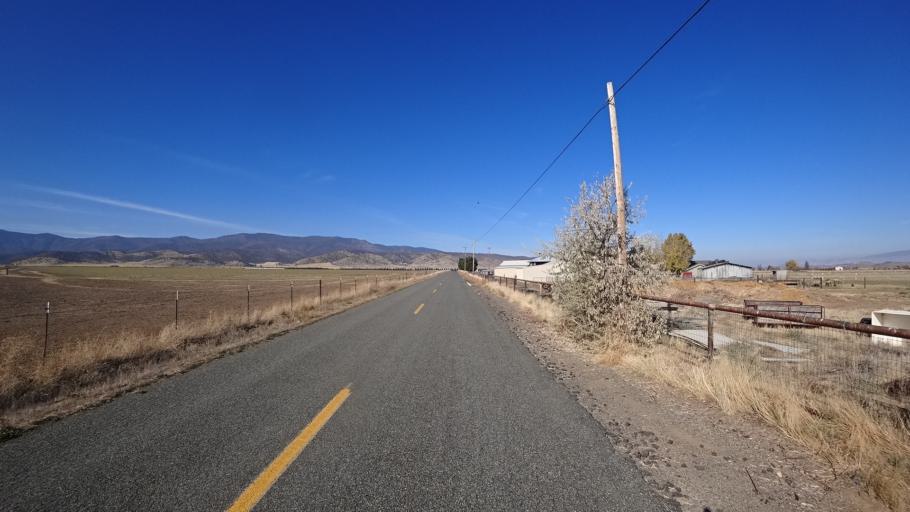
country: US
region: California
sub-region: Siskiyou County
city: Montague
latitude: 41.5451
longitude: -122.5401
